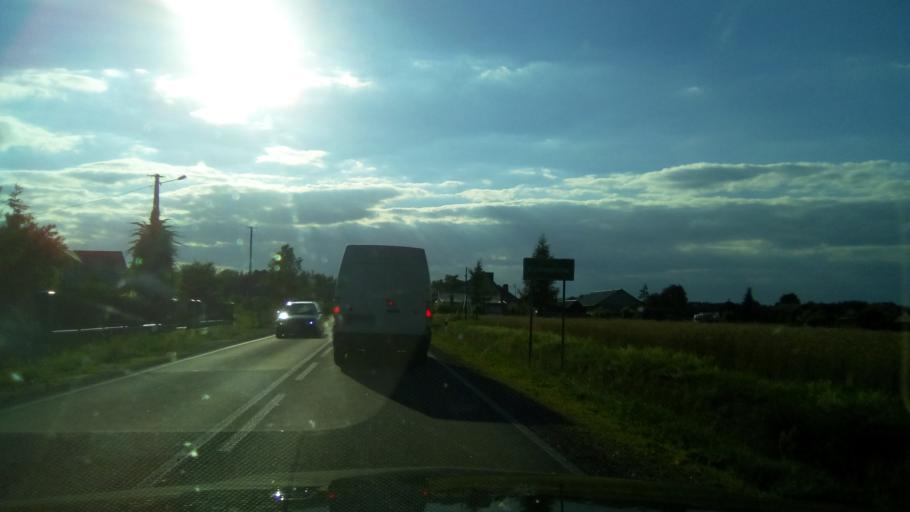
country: PL
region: Masovian Voivodeship
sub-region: Powiat bialobrzeski
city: Stromiec
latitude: 51.6443
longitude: 21.1443
